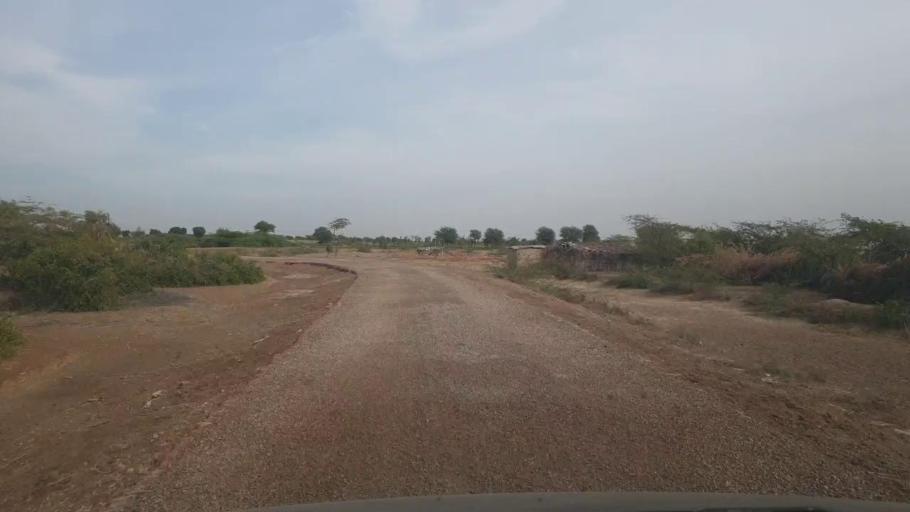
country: PK
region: Sindh
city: Kunri
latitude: 25.2902
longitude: 69.5819
